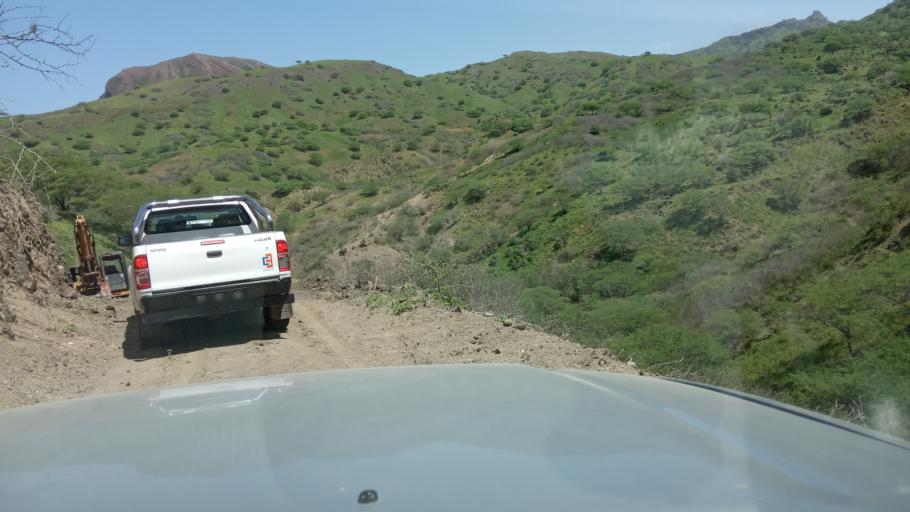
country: CV
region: Santa Catarina
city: Assomada
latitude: 15.1134
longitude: -23.7288
